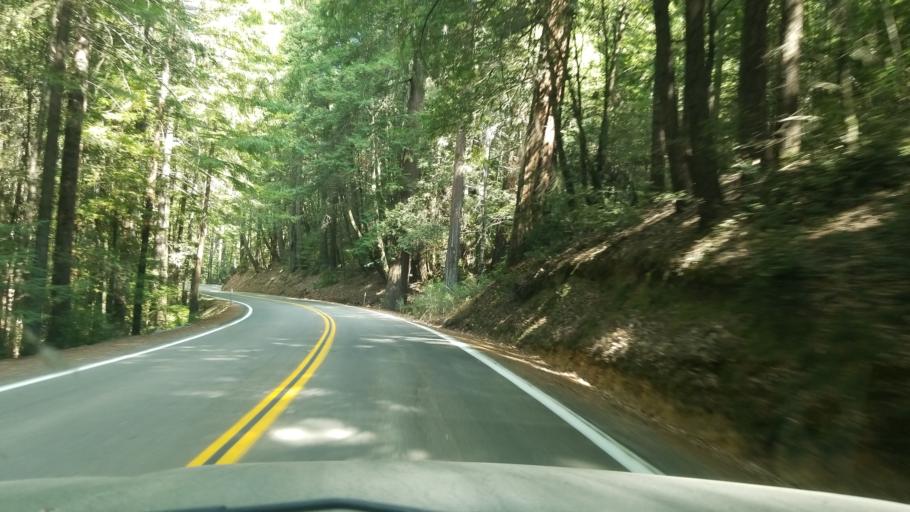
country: US
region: California
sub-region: Humboldt County
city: Redway
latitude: 39.8551
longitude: -123.7175
